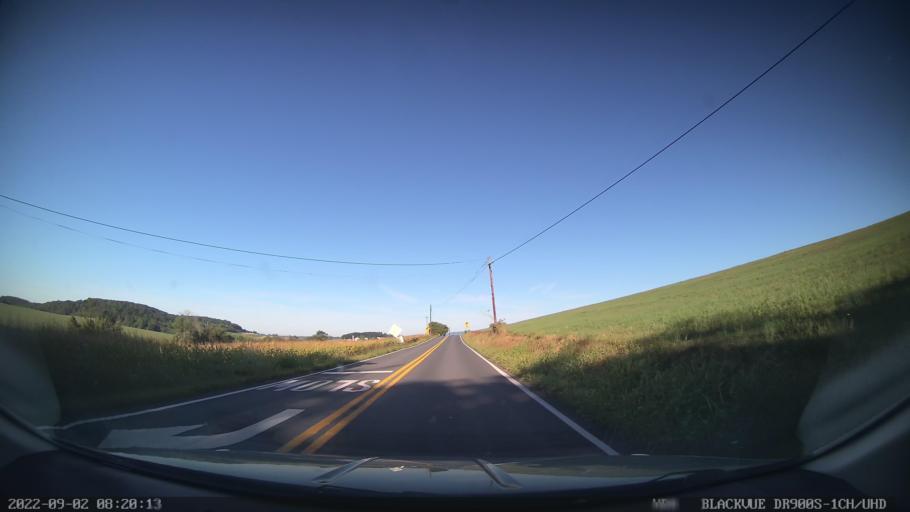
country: US
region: Pennsylvania
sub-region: Berks County
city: Shoemakersville
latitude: 40.5090
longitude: -75.9156
